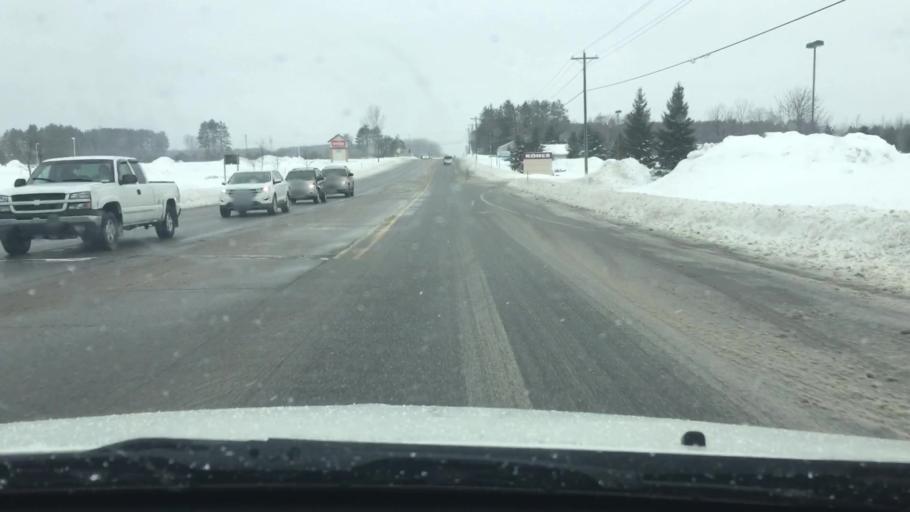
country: US
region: Michigan
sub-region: Otsego County
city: Gaylord
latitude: 45.0275
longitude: -84.7223
